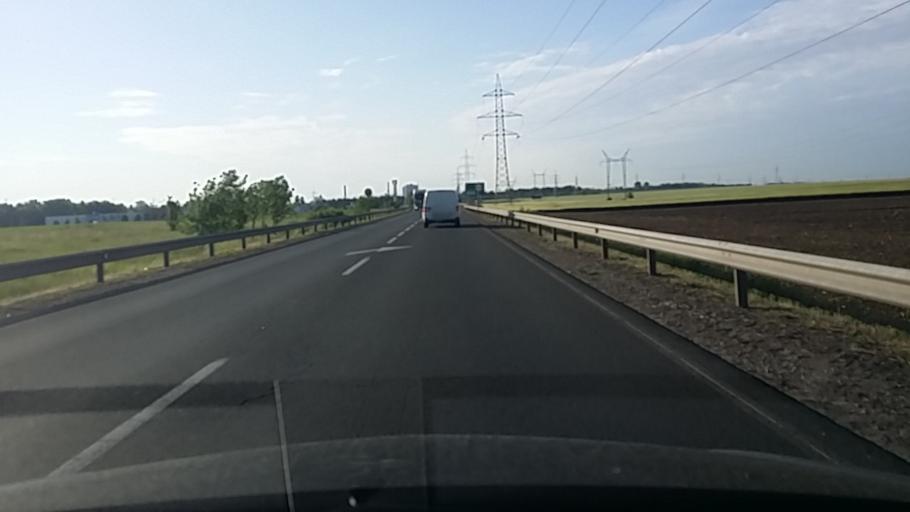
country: HU
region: Fejer
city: dunaujvaros
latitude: 46.9644
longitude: 18.9010
